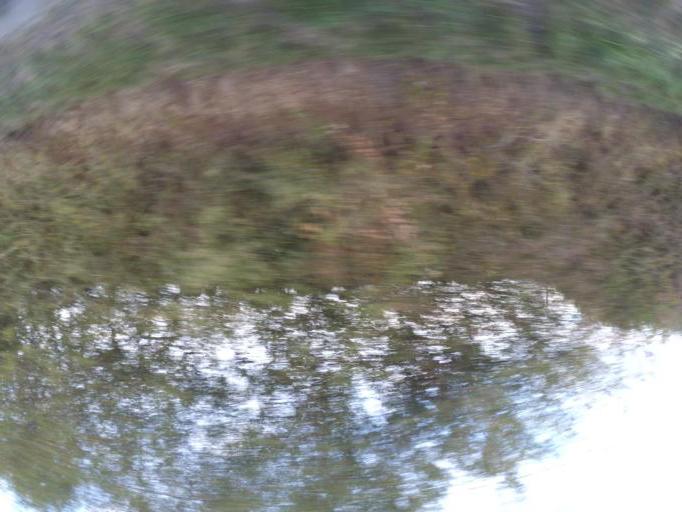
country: FR
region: Centre
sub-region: Departement d'Indre-et-Loire
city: Nazelles-Negron
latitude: 47.4474
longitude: 0.9601
